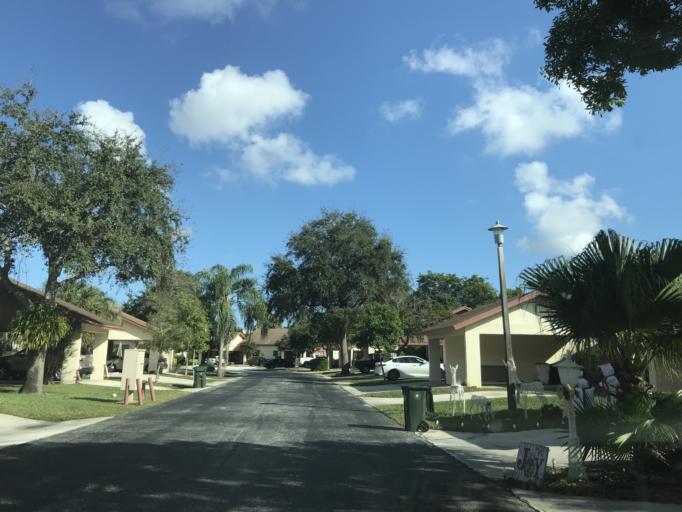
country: US
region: Florida
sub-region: Broward County
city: Coconut Creek
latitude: 26.2490
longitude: -80.1879
